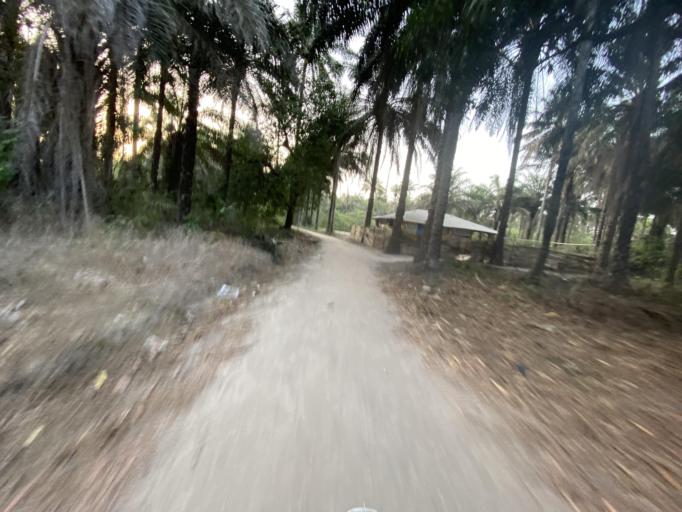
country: GW
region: Tombali
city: Quebo
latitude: 10.8938
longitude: -15.0106
